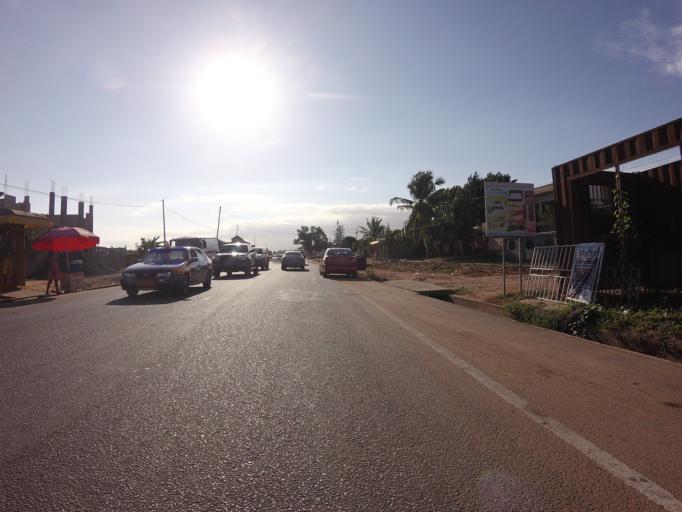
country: GH
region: Greater Accra
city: Nungua
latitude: 5.6446
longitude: -0.0768
